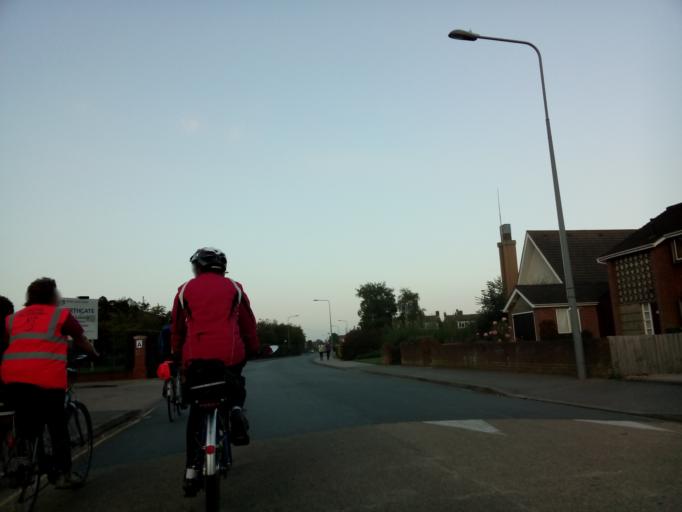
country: GB
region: England
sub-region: Suffolk
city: Ipswich
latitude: 52.0710
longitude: 1.1789
